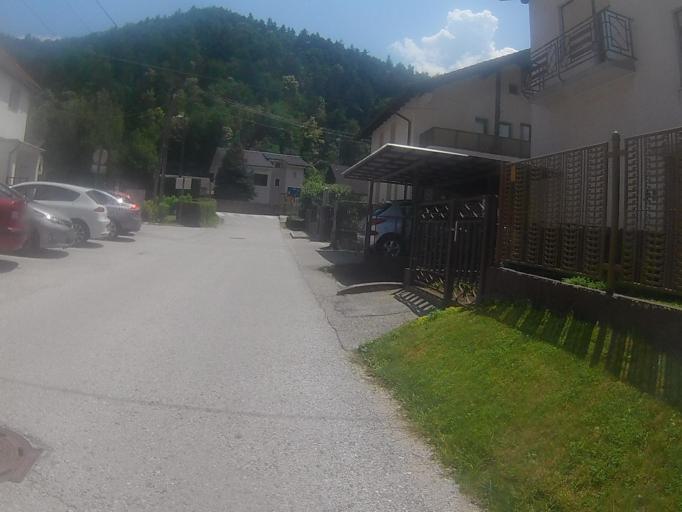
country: SI
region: Ruse
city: Bistrica ob Dravi
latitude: 46.5561
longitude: 15.5547
